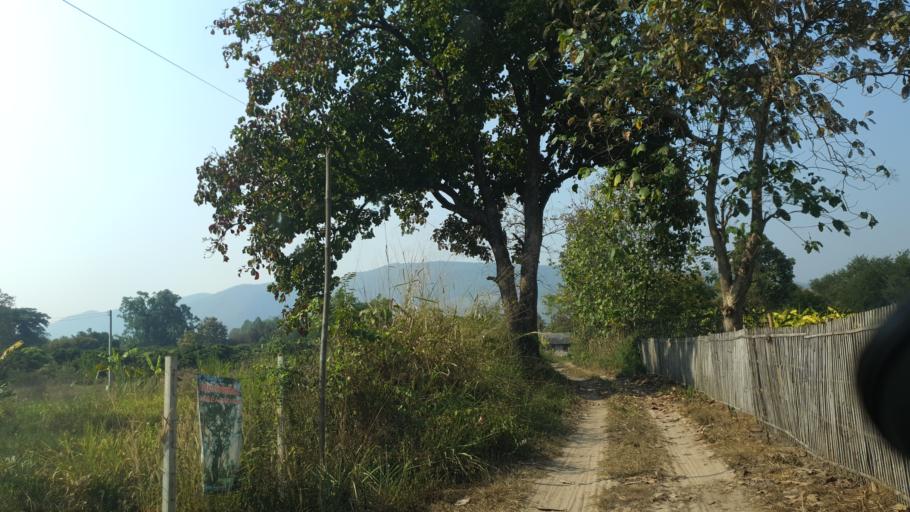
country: TH
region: Chiang Mai
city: Mae On
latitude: 18.7476
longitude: 99.2484
